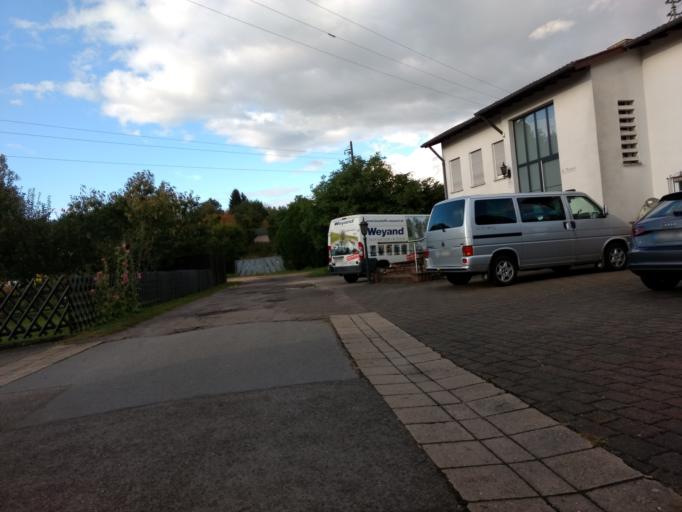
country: DE
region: Saarland
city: Schmelz
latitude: 49.3934
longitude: 6.8393
